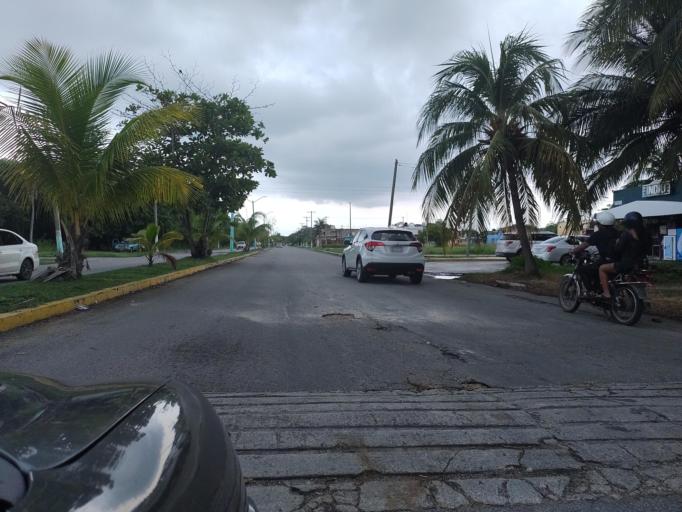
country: MX
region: Quintana Roo
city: Chetumal
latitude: 18.5088
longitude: -88.2827
